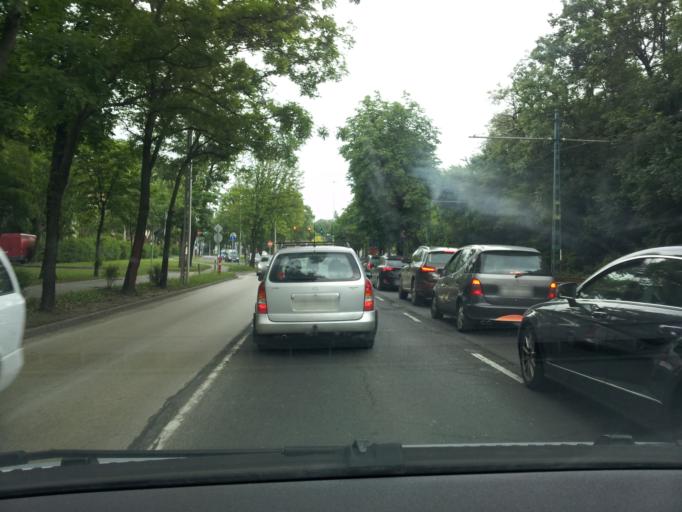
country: HU
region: Budapest
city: Budapest XII. keruelet
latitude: 47.5111
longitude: 19.0070
